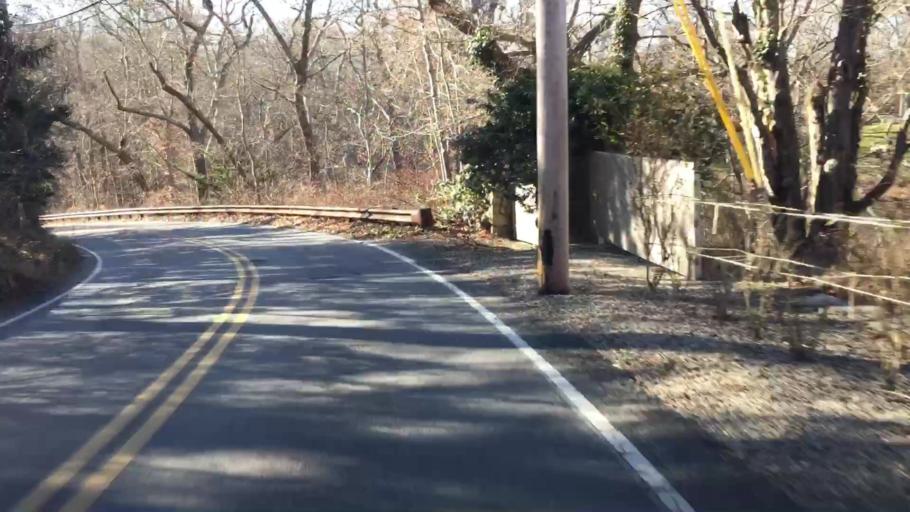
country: US
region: Massachusetts
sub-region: Barnstable County
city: Falmouth
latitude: 41.5372
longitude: -70.6558
